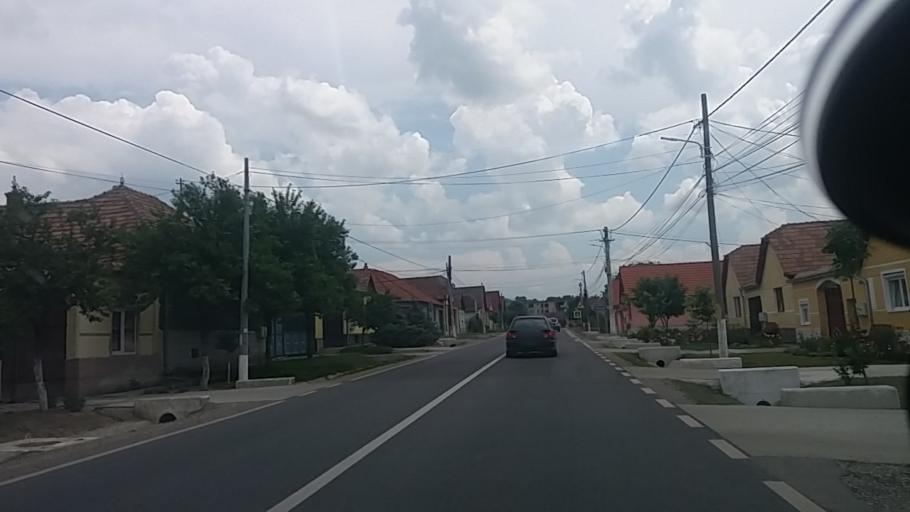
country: RO
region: Sibiu
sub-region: Comuna Slimnic
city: Slimnic
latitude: 45.9650
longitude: 24.1611
